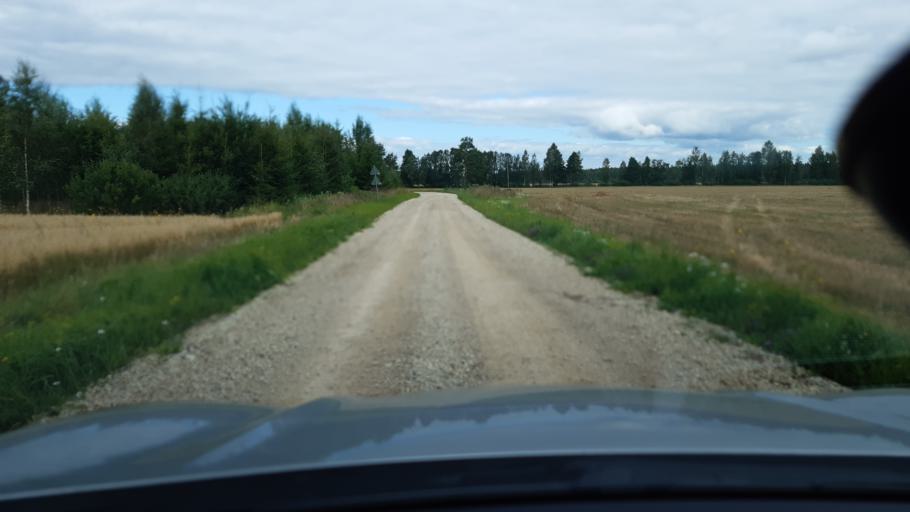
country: EE
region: Raplamaa
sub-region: Jaervakandi vald
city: Jarvakandi
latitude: 58.7986
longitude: 24.8619
